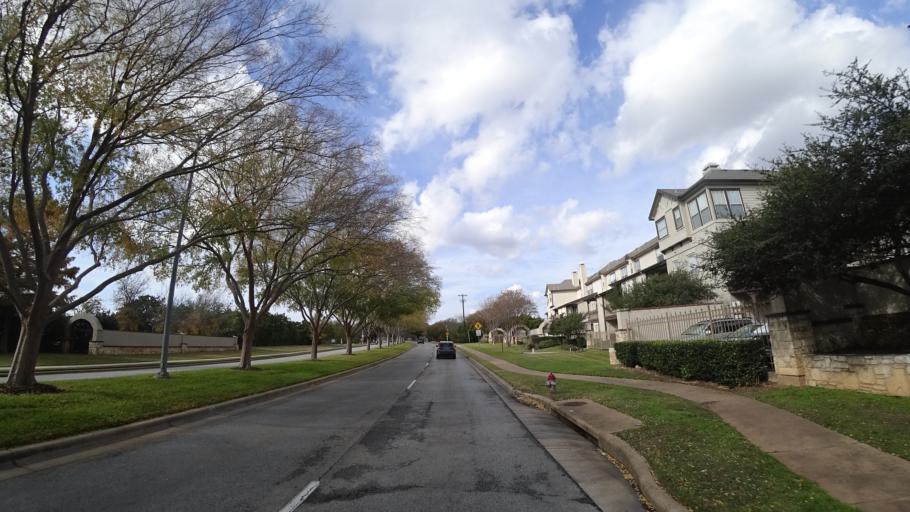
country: US
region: Texas
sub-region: Williamson County
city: Brushy Creek
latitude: 30.5010
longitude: -97.7248
